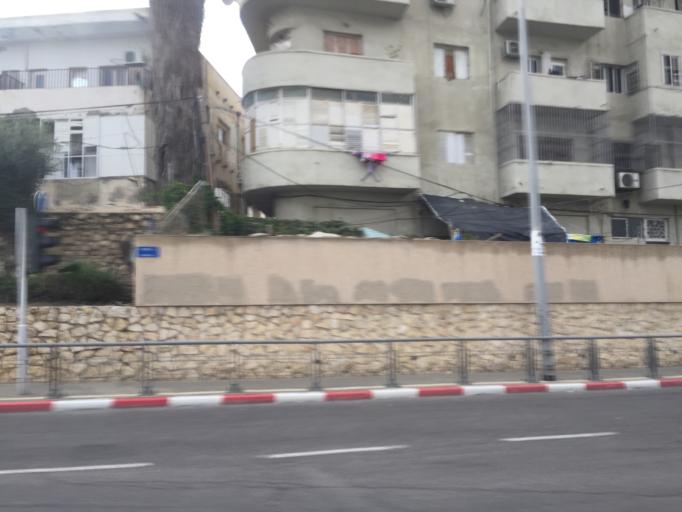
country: IL
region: Tel Aviv
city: Tel Aviv
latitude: 32.0586
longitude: 34.7840
